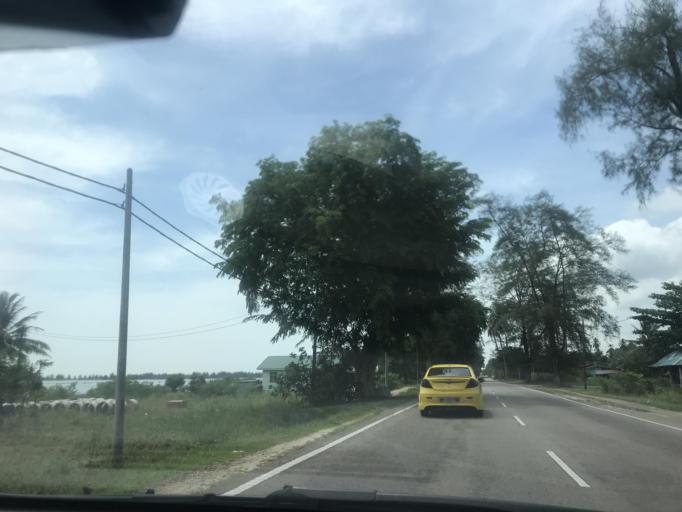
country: MY
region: Kelantan
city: Tumpat
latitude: 6.2101
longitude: 102.1356
